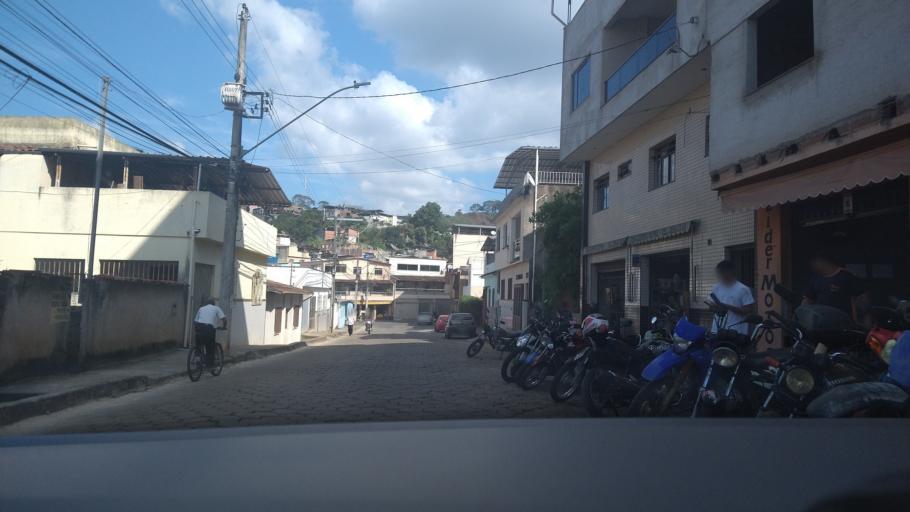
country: BR
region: Minas Gerais
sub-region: Vicosa
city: Vicosa
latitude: -20.7674
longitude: -42.8875
